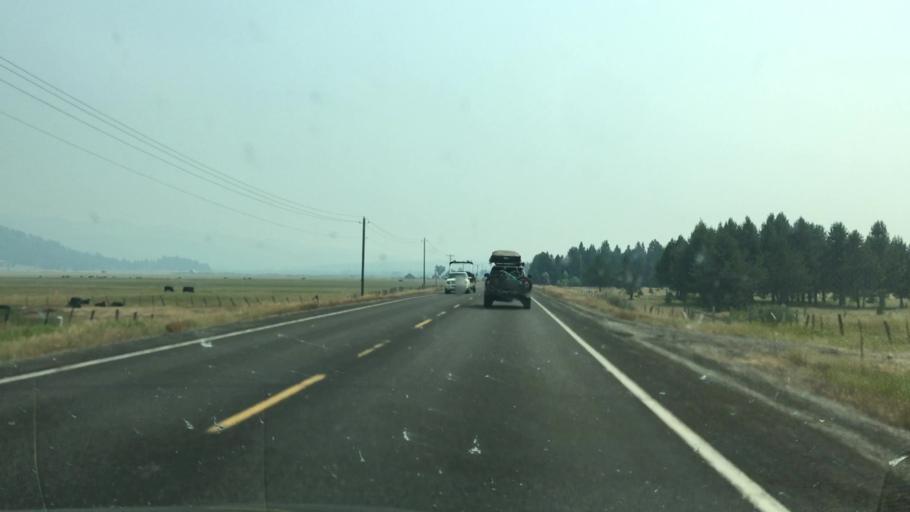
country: US
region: Idaho
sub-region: Valley County
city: Cascade
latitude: 44.4406
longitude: -115.9995
